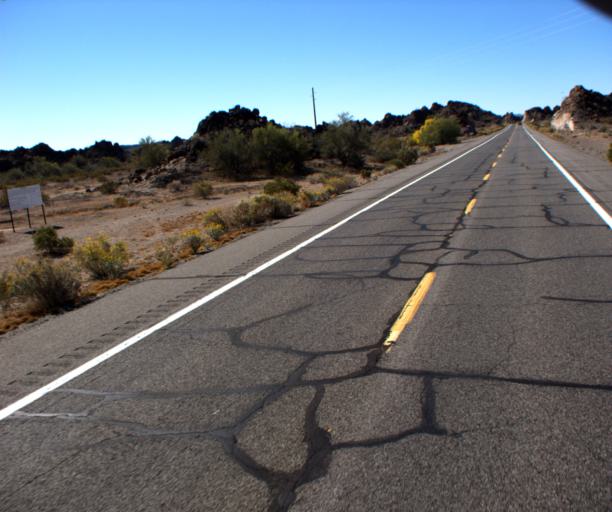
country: US
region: Arizona
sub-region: Pima County
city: Ajo
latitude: 32.5561
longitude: -112.8792
